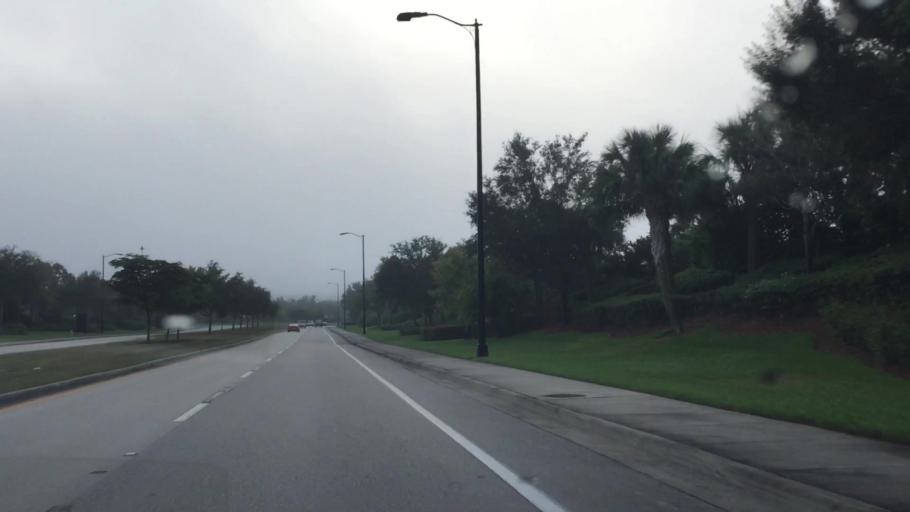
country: US
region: Florida
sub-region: Lee County
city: Gateway
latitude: 26.5814
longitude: -81.7825
